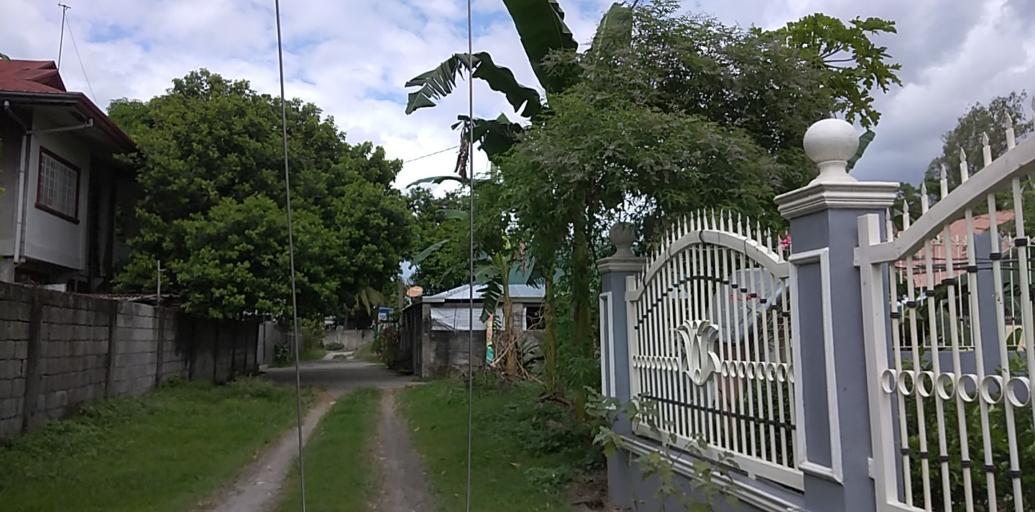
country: PH
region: Central Luzon
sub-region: Province of Pampanga
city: Porac
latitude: 15.0616
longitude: 120.5431
